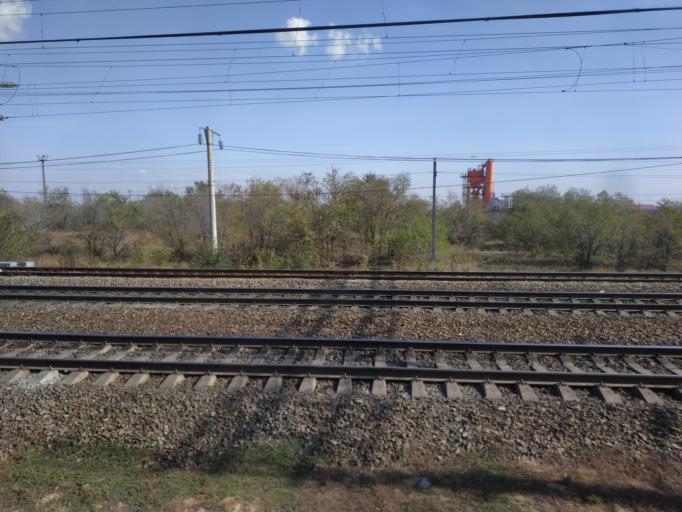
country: RU
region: Volgograd
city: Gumrak
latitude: 48.7922
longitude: 44.3659
